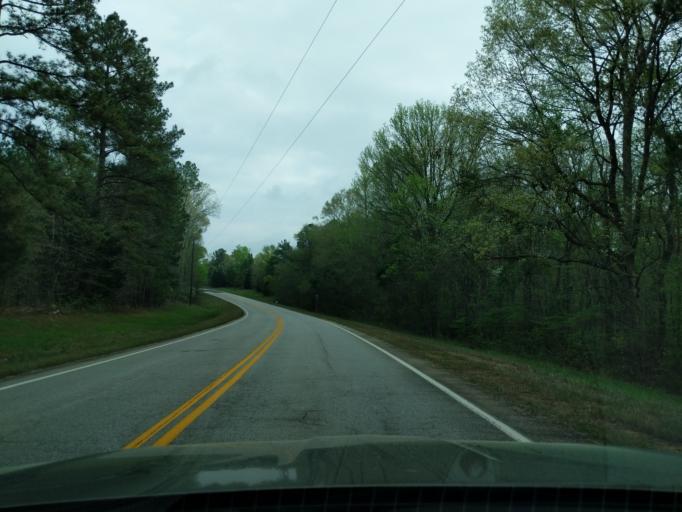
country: US
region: Georgia
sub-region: Lincoln County
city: Lincolnton
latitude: 33.7585
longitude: -82.3797
